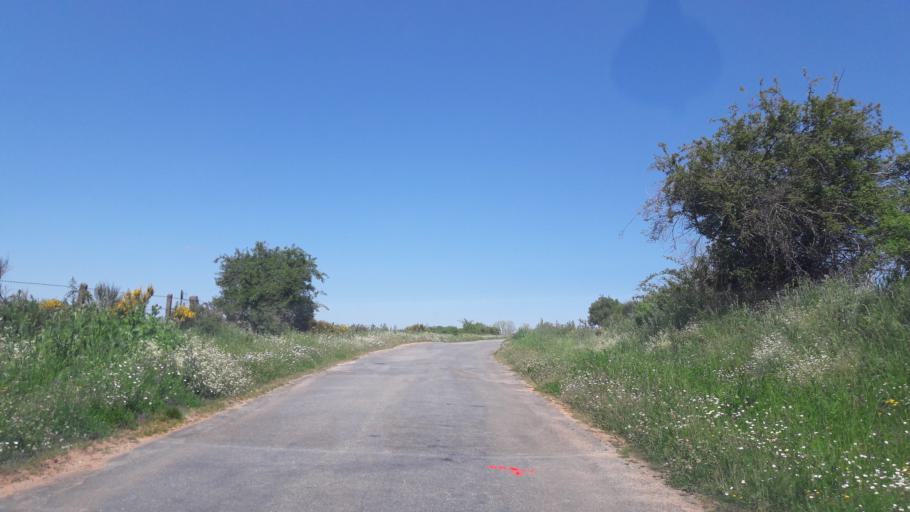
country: ES
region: Castille and Leon
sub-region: Provincia de Salamanca
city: Endrinal
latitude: 40.5780
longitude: -5.8071
